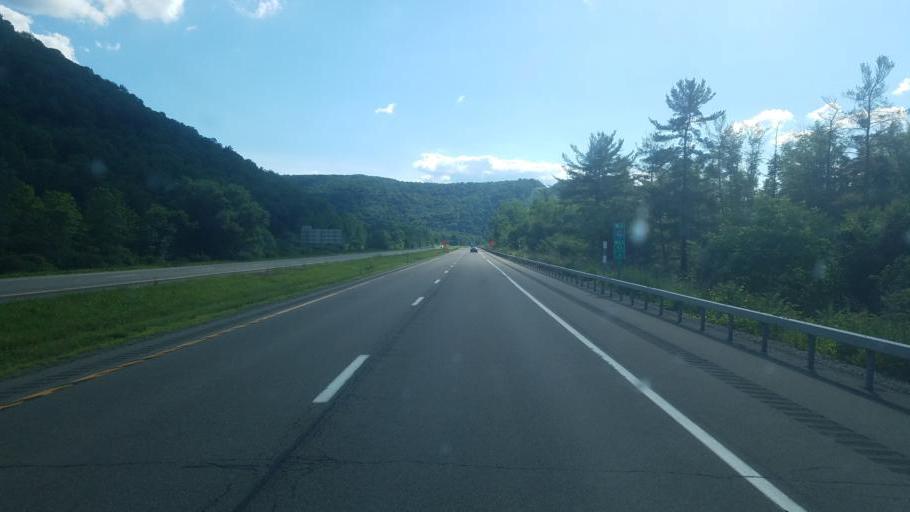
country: US
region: New York
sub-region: Cattaraugus County
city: Salamanca
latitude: 42.1035
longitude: -78.7971
